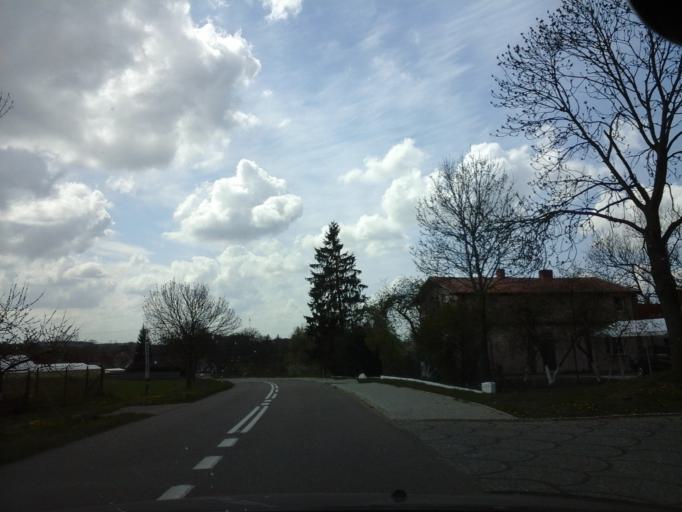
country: PL
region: West Pomeranian Voivodeship
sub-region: Powiat stargardzki
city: Suchan
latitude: 53.2852
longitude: 15.3338
